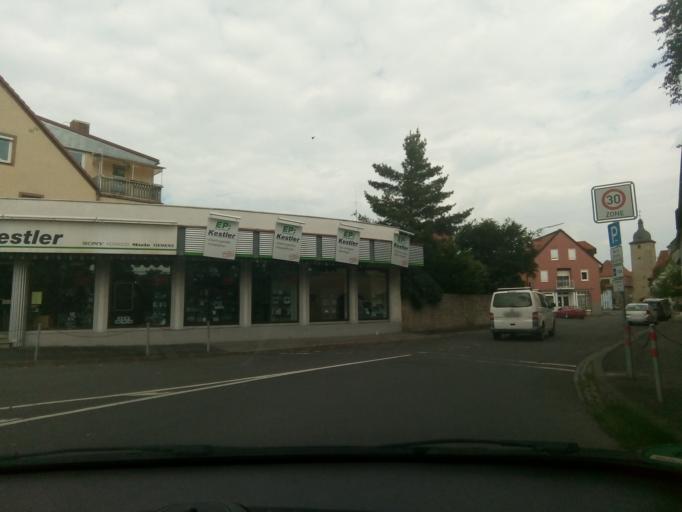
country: DE
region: Bavaria
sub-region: Regierungsbezirk Unterfranken
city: Volkach
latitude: 49.8680
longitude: 10.2231
